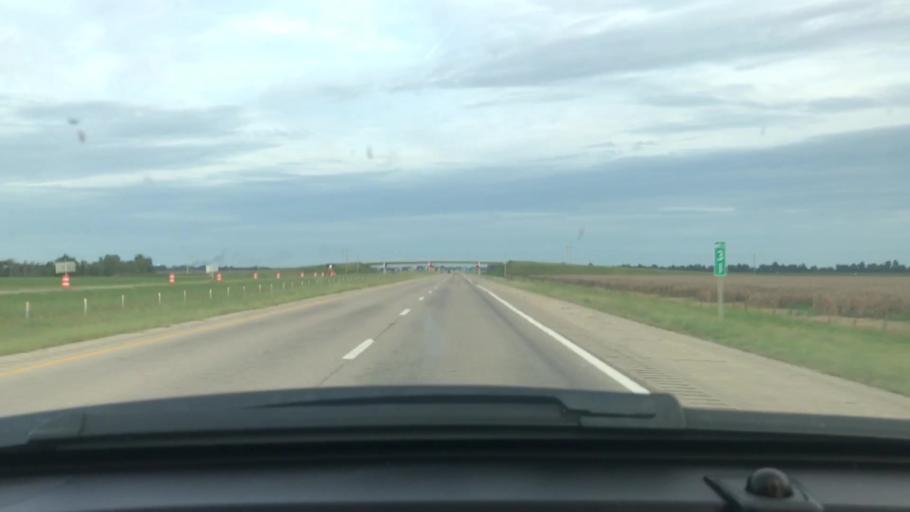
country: US
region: Arkansas
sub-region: Craighead County
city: Bay
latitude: 35.7085
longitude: -90.5704
